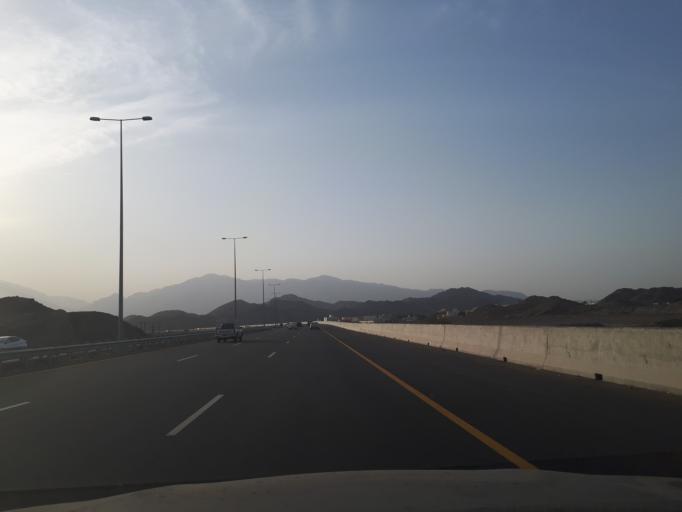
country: OM
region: Muhafazat ad Dakhiliyah
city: Bidbid
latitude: 23.3390
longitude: 58.1096
